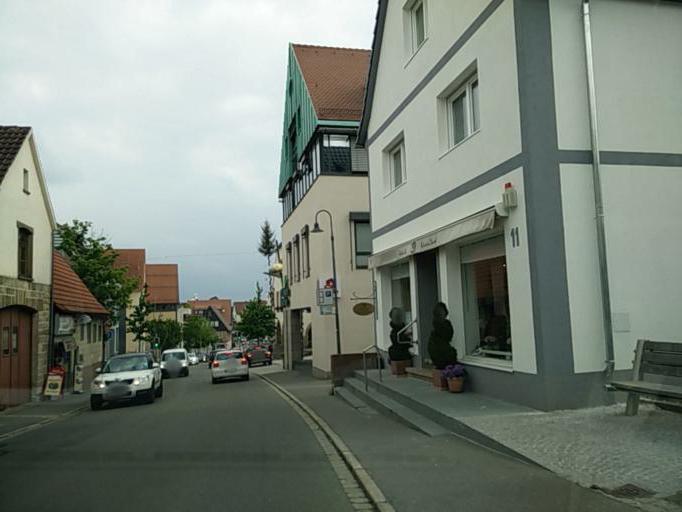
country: DE
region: Baden-Wuerttemberg
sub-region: Regierungsbezirk Stuttgart
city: Holzgerlingen
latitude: 48.6405
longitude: 9.0116
